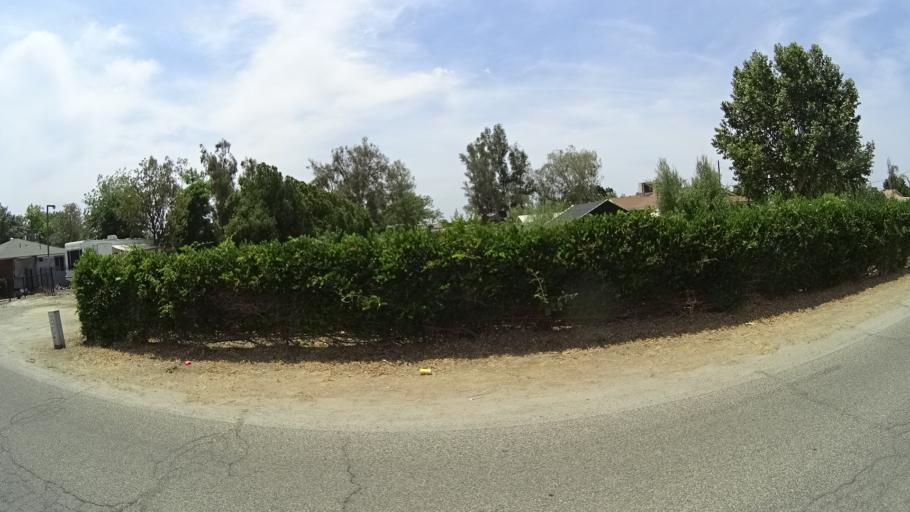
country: US
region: California
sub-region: Fresno County
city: West Park
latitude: 36.7526
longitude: -119.8532
